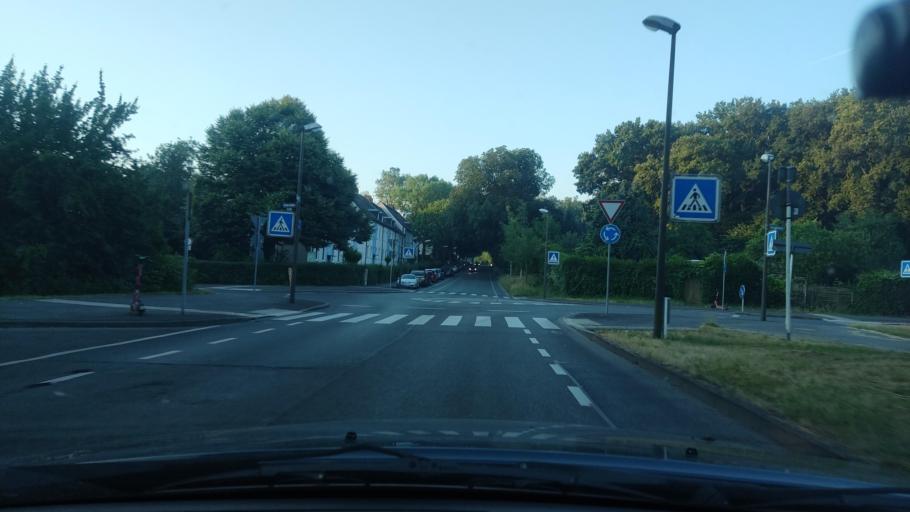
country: DE
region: North Rhine-Westphalia
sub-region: Regierungsbezirk Arnsberg
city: Dortmund
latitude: 51.5442
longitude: 7.4739
